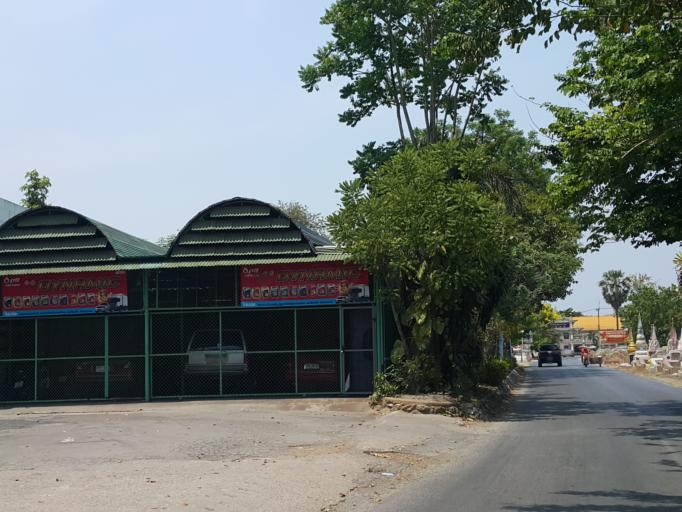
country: TH
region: Kanchanaburi
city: Kanchanaburi
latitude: 14.0302
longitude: 99.5278
